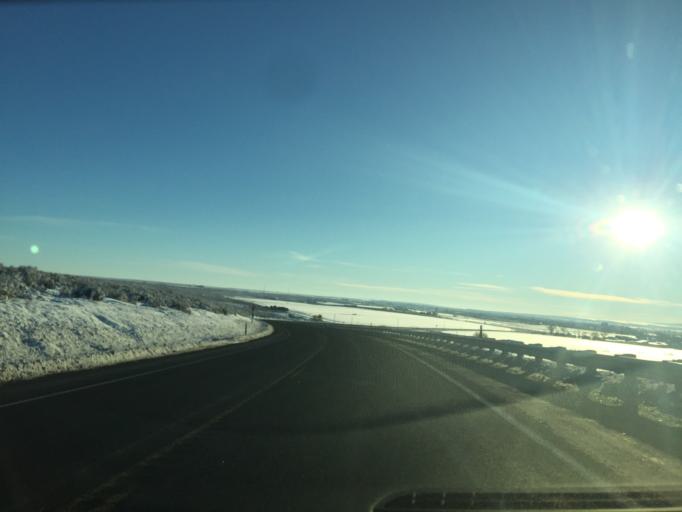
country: US
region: Washington
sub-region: Grant County
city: Soap Lake
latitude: 47.6464
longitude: -119.2548
